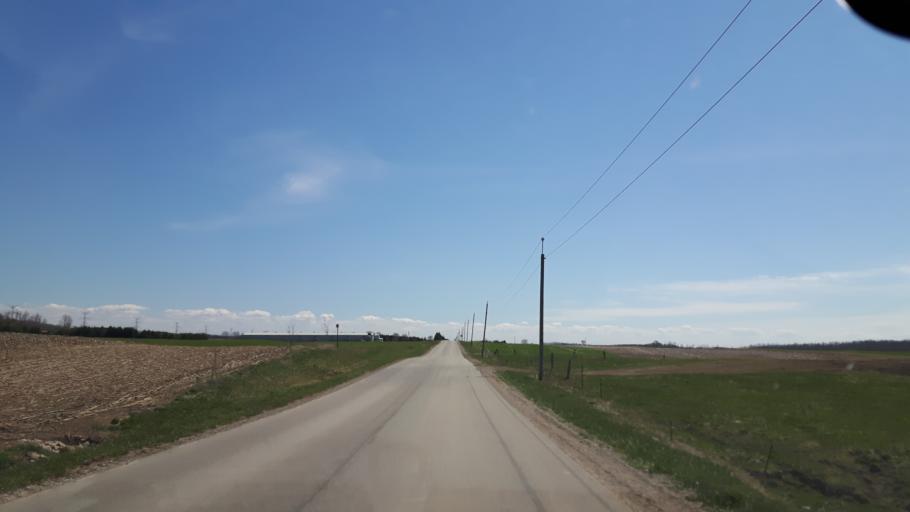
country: CA
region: Ontario
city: Goderich
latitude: 43.6489
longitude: -81.6441
